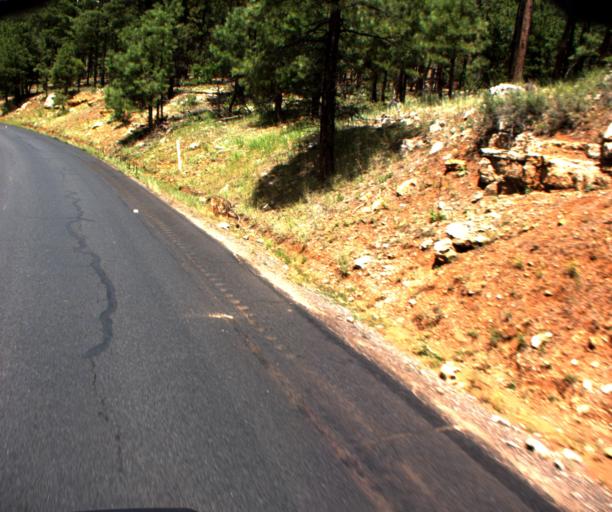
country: US
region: Arizona
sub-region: Gila County
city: Pine
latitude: 34.4584
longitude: -111.4382
